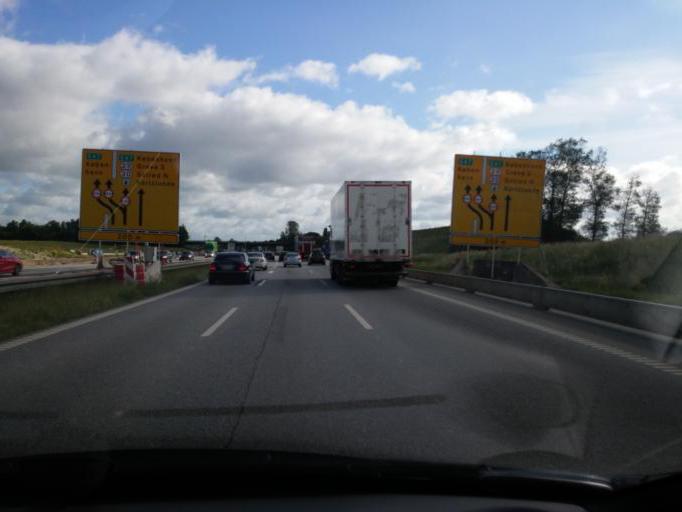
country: DK
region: Zealand
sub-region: Solrod Kommune
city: Solrod
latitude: 55.5185
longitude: 12.1914
